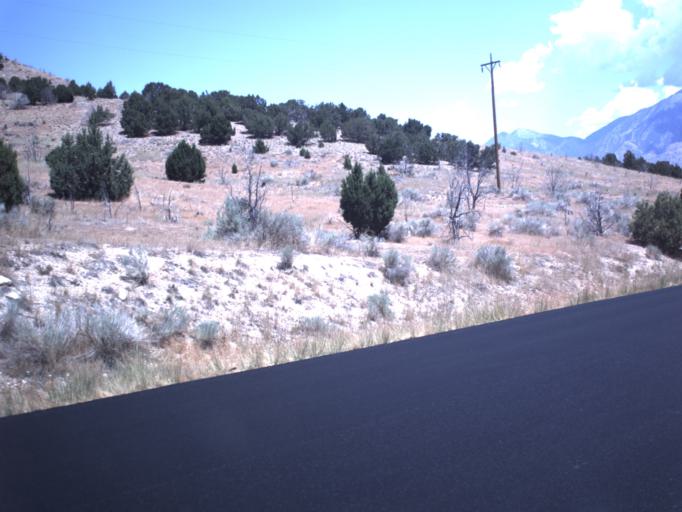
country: US
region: Utah
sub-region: Juab County
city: Nephi
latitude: 39.6995
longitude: -111.9354
